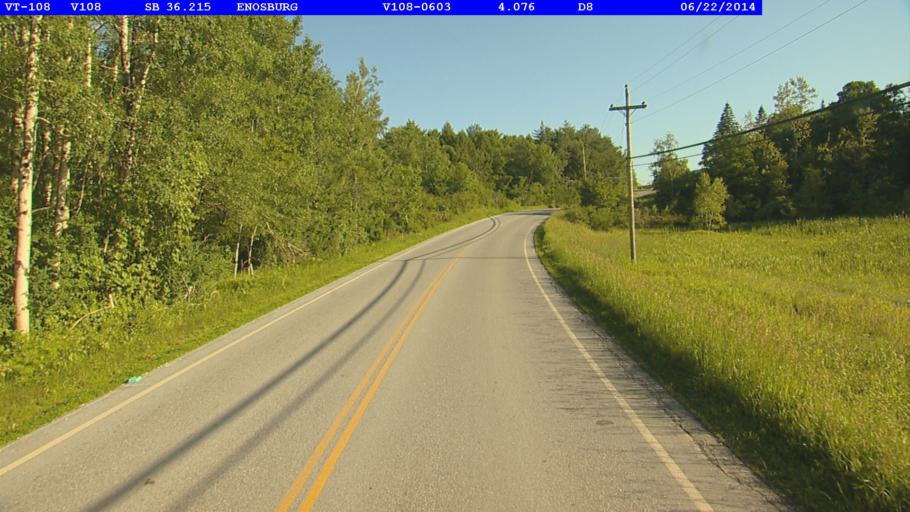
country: US
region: Vermont
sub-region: Franklin County
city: Enosburg Falls
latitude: 44.8941
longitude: -72.8006
